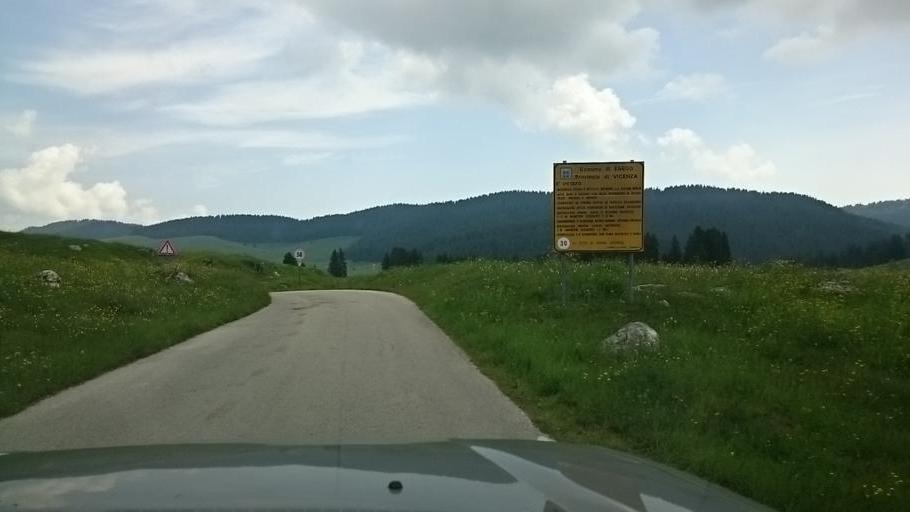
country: IT
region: Veneto
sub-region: Provincia di Vicenza
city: Foza
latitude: 45.9415
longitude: 11.6102
